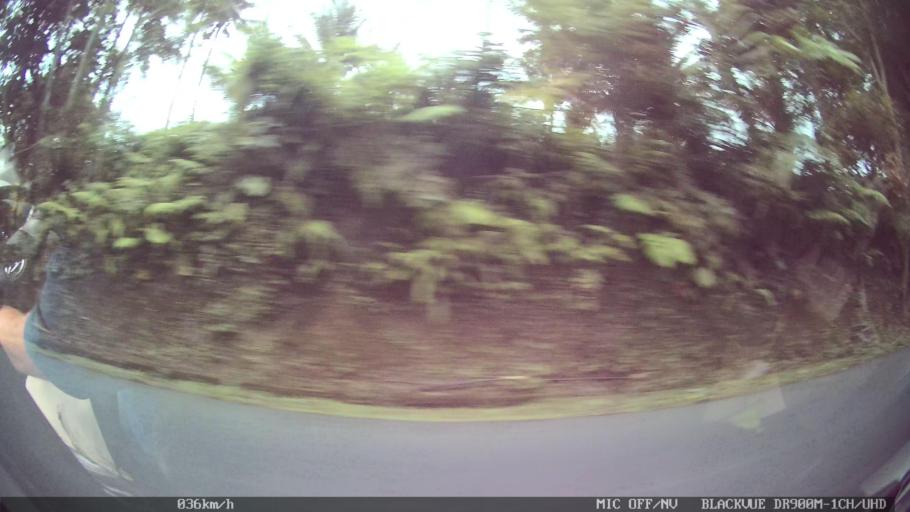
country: ID
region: Bali
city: Banjar Brahmanabukit
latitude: -8.4448
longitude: 115.3613
